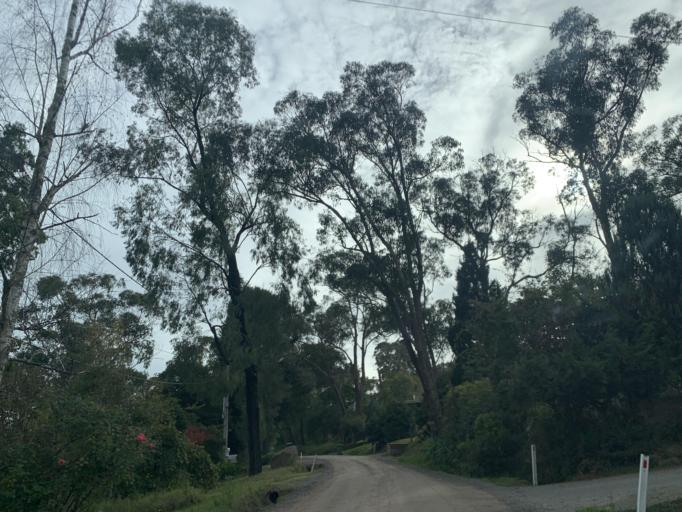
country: AU
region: Victoria
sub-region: Yarra Ranges
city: Belgrave South
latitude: -37.9248
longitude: 145.3412
